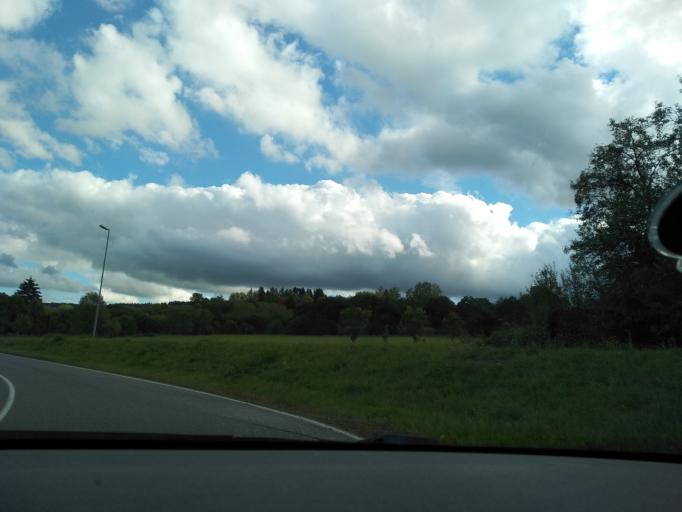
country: DE
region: Hesse
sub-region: Regierungsbezirk Giessen
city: Haiger
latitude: 50.7456
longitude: 8.1917
